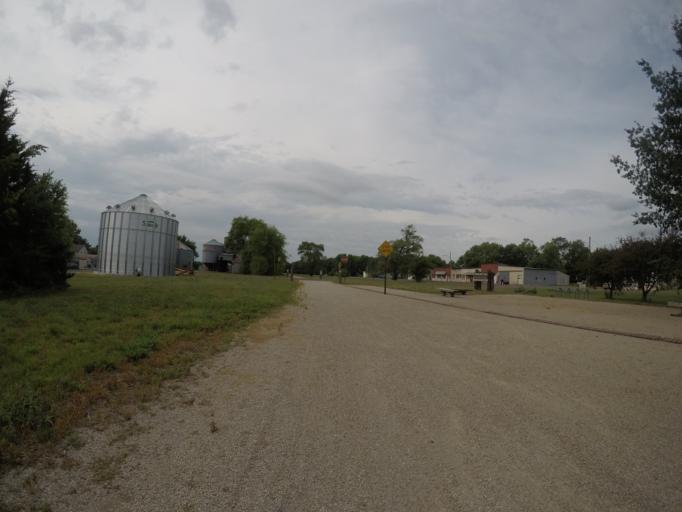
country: US
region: Kansas
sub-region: Franklin County
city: Ottawa
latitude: 38.4894
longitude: -95.2743
